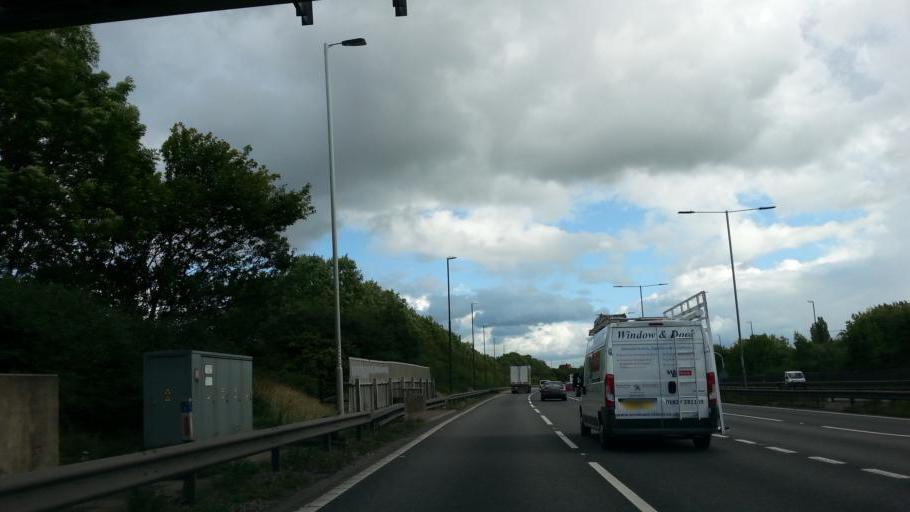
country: GB
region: England
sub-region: Warwickshire
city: Water Orton
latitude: 52.5124
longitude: -1.7515
